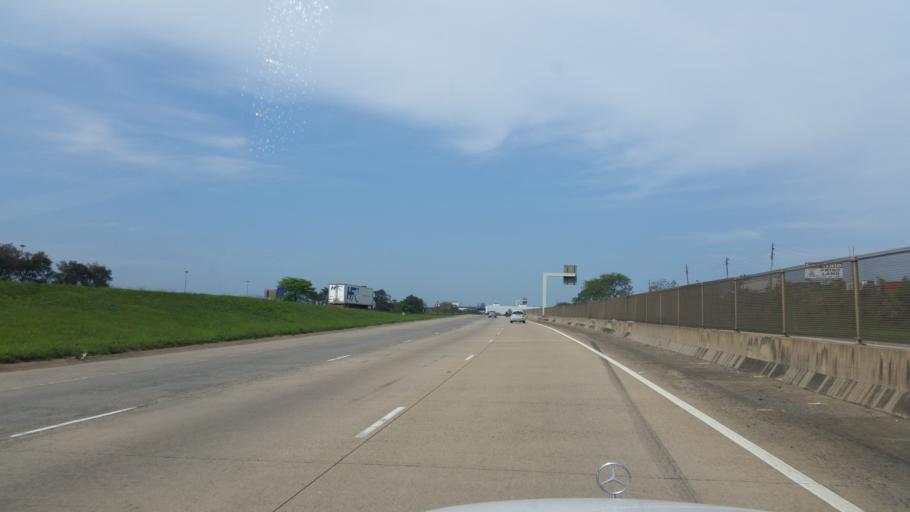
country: ZA
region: KwaZulu-Natal
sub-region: uMgungundlovu District Municipality
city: Camperdown
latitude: -29.7342
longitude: 30.5844
